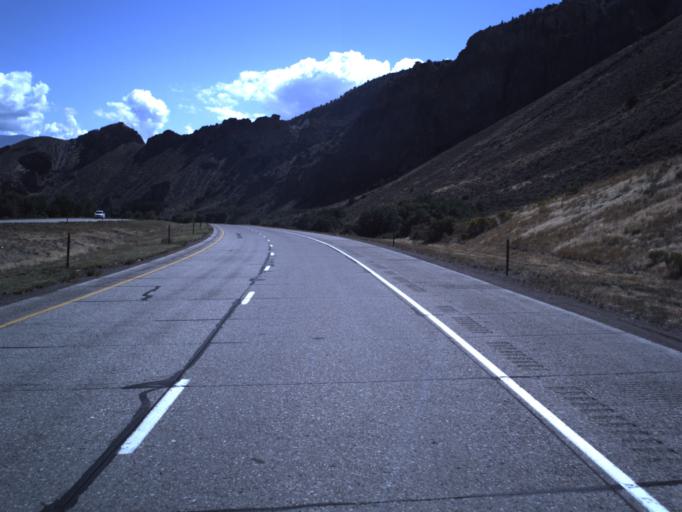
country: US
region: Utah
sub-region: Sevier County
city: Monroe
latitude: 38.5791
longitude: -112.2905
